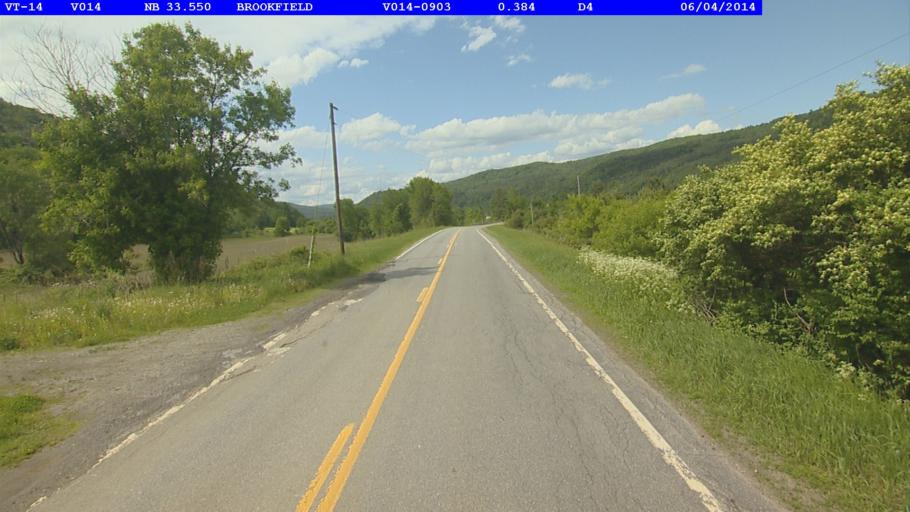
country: US
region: Vermont
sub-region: Orange County
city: Chelsea
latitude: 43.9846
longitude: -72.5572
